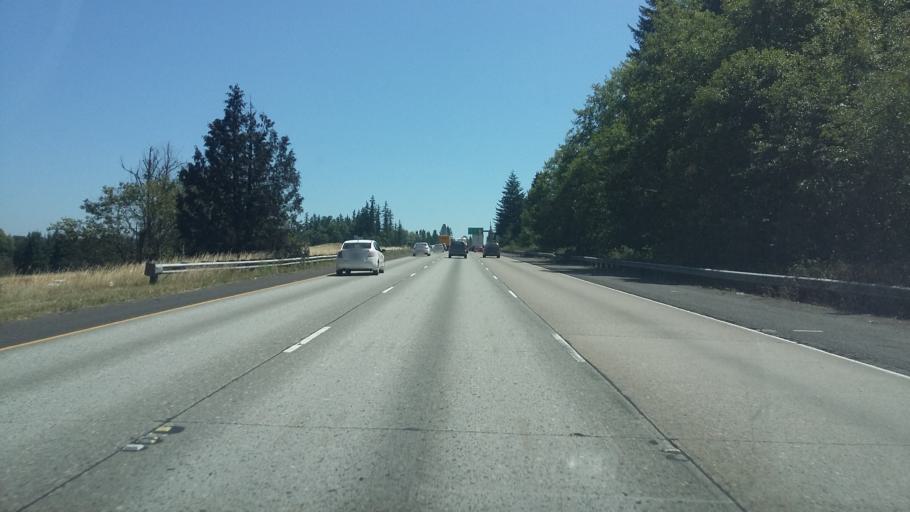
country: US
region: Washington
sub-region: Clark County
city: Mount Vista
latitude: 45.7753
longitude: -122.6713
